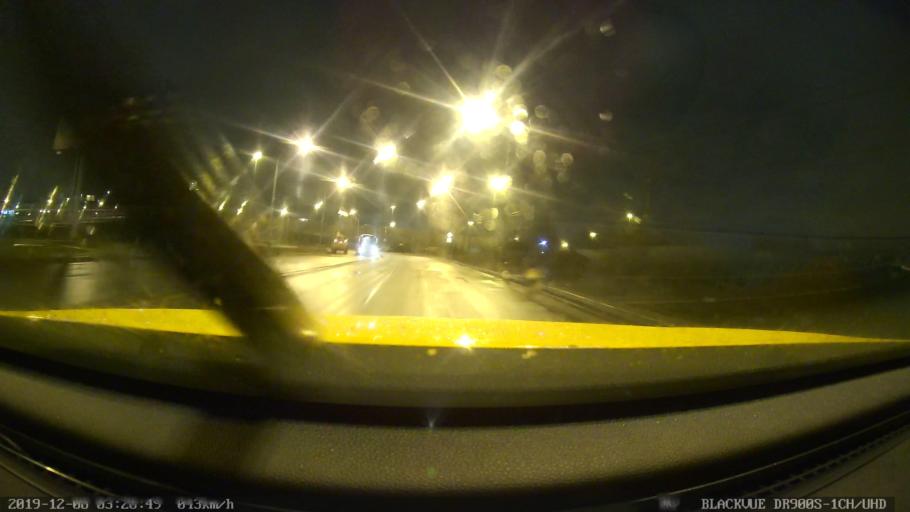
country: RU
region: Moskovskaya
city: Mosrentgen
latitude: 55.6245
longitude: 37.4265
